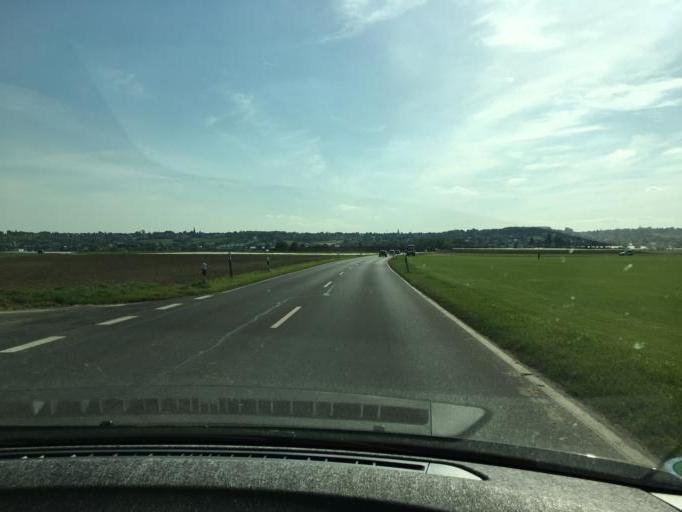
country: DE
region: North Rhine-Westphalia
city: Bornheim
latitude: 50.7824
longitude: 6.9474
